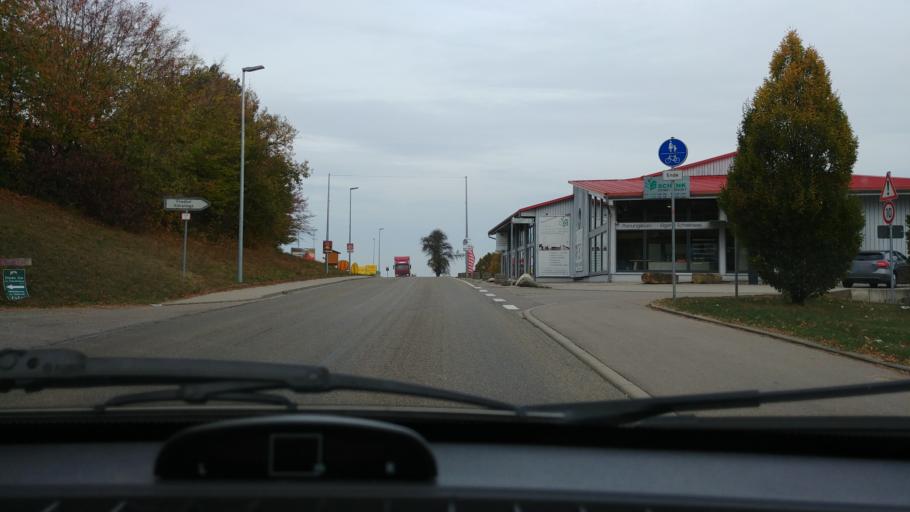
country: DE
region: Baden-Wuerttemberg
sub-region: Regierungsbezirk Stuttgart
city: Jagstzell
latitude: 49.0330
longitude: 10.0974
